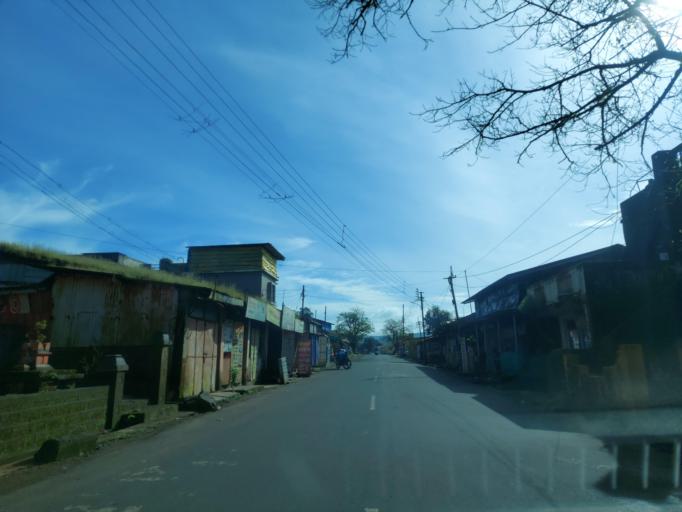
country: IN
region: Maharashtra
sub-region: Sindhudurg
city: Savantvadi
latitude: 15.9623
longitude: 73.9971
